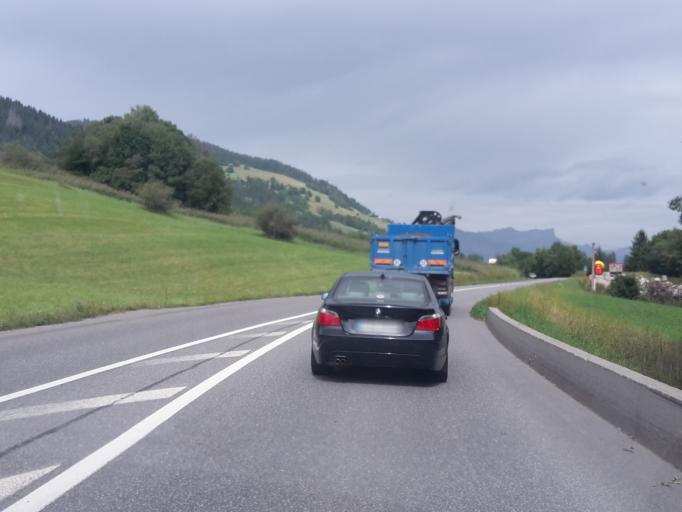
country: FR
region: Rhone-Alpes
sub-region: Departement de la Haute-Savoie
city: Praz-sur-Arly
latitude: 45.8437
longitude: 6.5907
